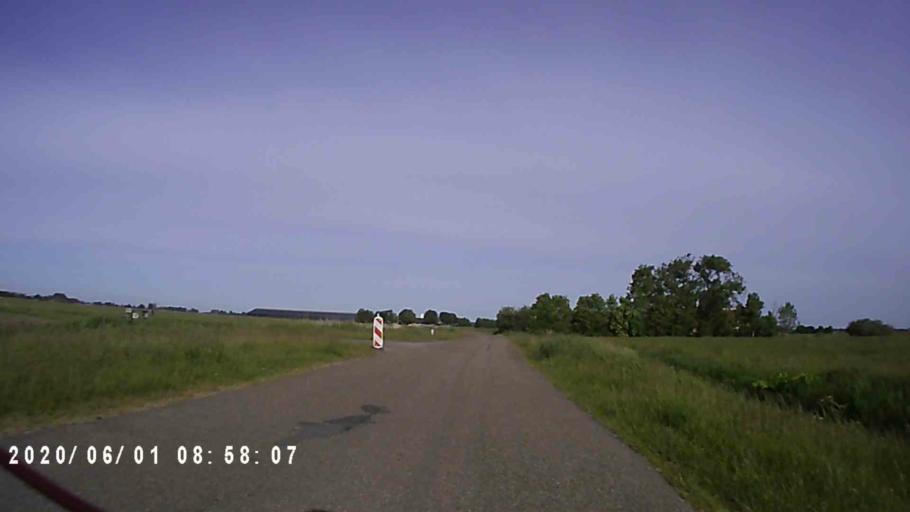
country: NL
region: Friesland
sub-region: Gemeente Ferwerderadiel
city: Hallum
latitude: 53.2813
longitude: 5.8077
